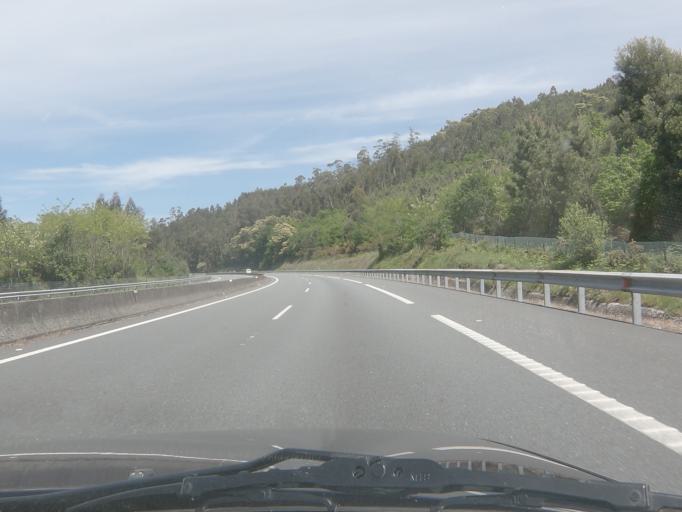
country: ES
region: Galicia
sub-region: Provincia da Coruna
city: Padron
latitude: 42.7627
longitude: -8.6450
